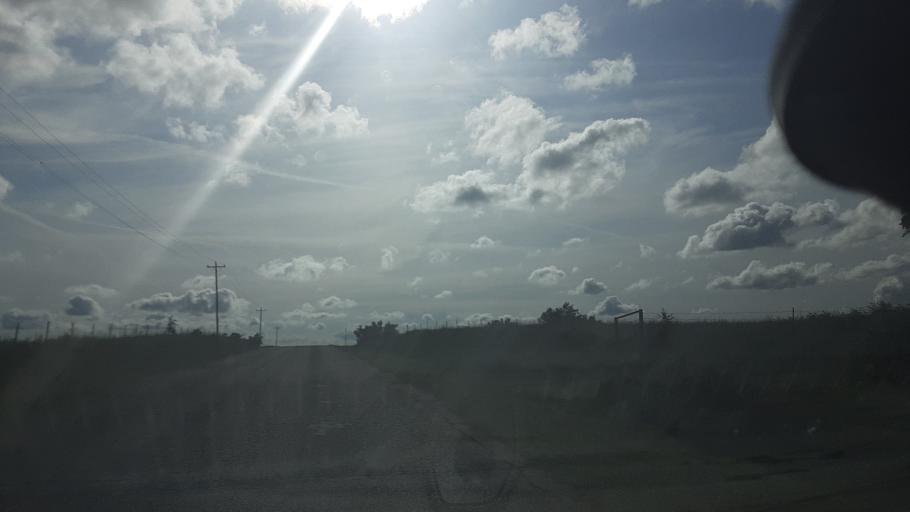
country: US
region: Oklahoma
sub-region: Logan County
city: Langston
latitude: 36.0578
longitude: -97.3790
